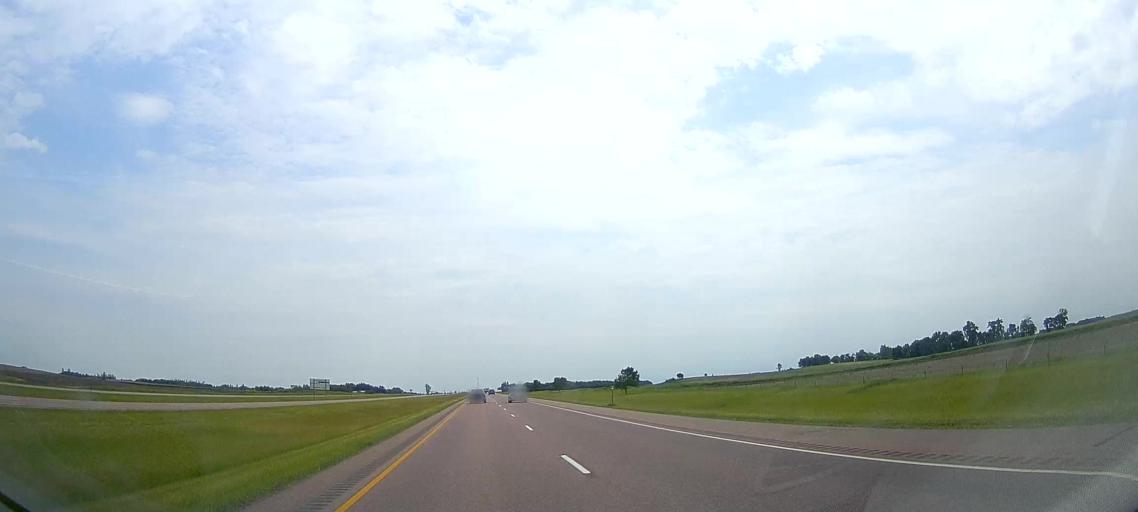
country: US
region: South Dakota
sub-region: Minnehaha County
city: Hartford
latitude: 43.6536
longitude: -97.1026
